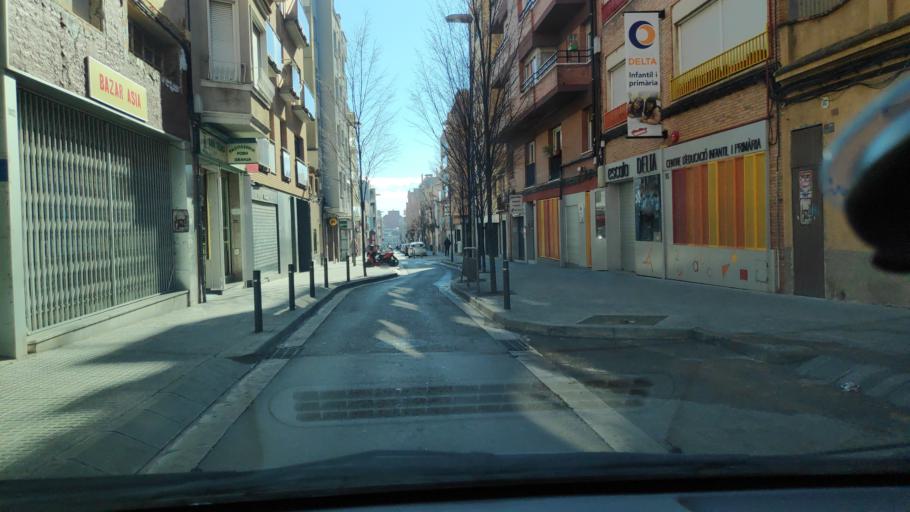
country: ES
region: Catalonia
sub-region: Provincia de Barcelona
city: Terrassa
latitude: 41.5727
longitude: 2.0179
